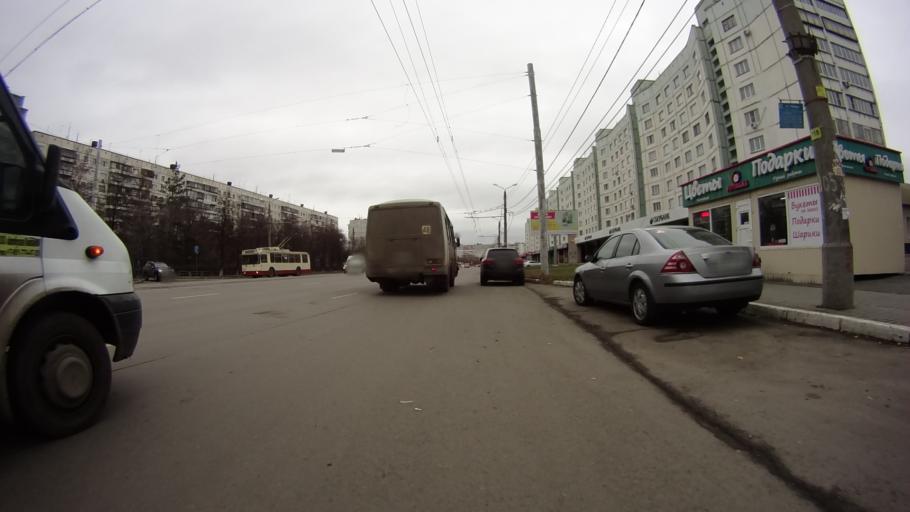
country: RU
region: Chelyabinsk
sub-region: Gorod Chelyabinsk
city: Chelyabinsk
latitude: 55.1944
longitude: 61.3477
